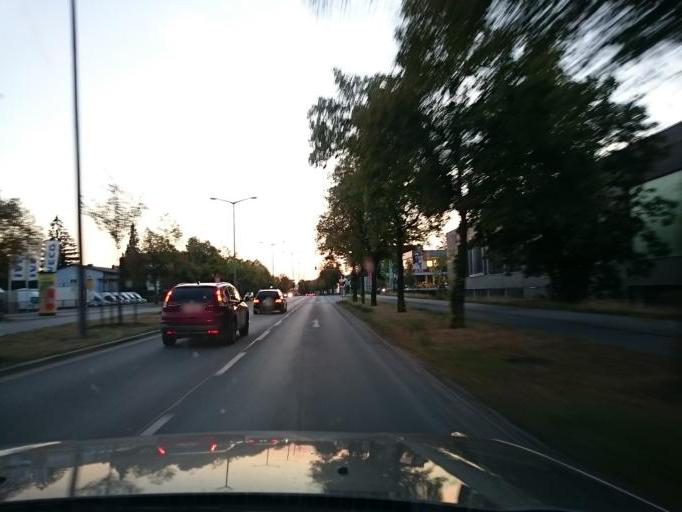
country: DE
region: Bavaria
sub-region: Upper Palatinate
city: Regensburg
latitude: 49.0280
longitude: 12.1119
